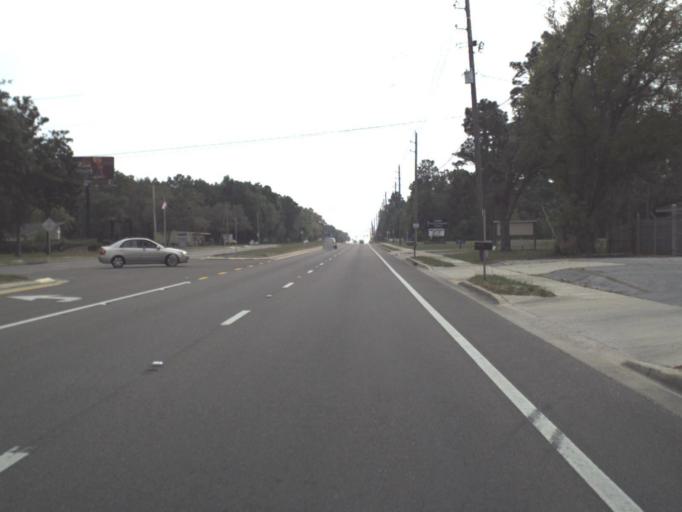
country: US
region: Florida
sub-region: Santa Rosa County
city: Milton
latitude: 30.6537
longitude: -87.0553
